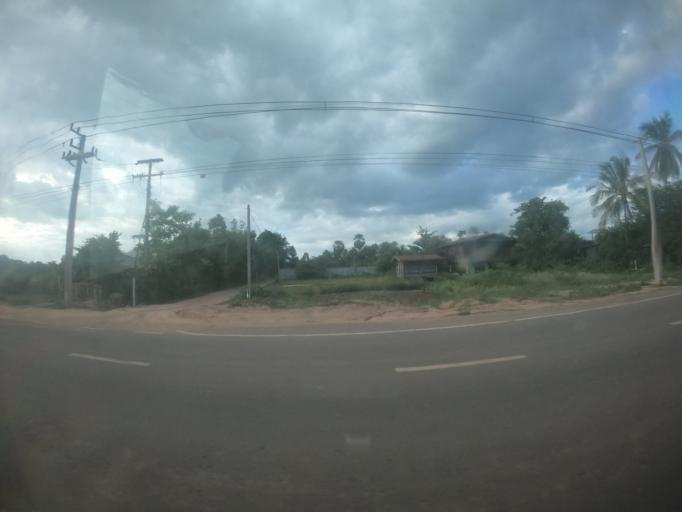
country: TH
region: Surin
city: Kap Choeng
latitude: 14.4559
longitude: 103.6794
